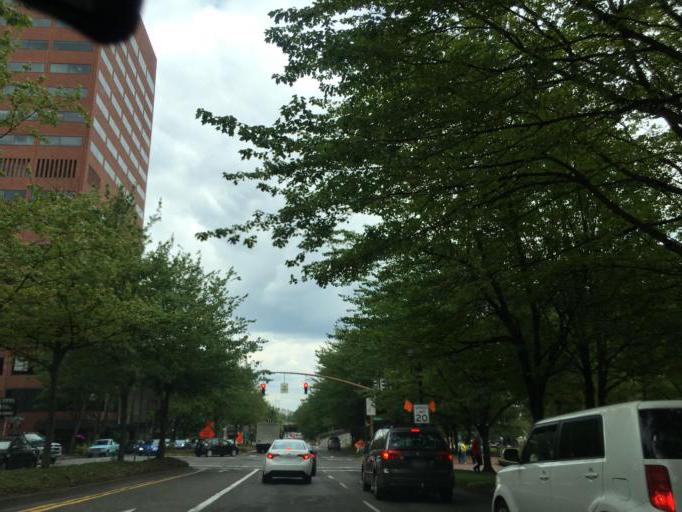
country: US
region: Oregon
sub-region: Multnomah County
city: Portland
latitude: 45.5124
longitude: -122.6752
